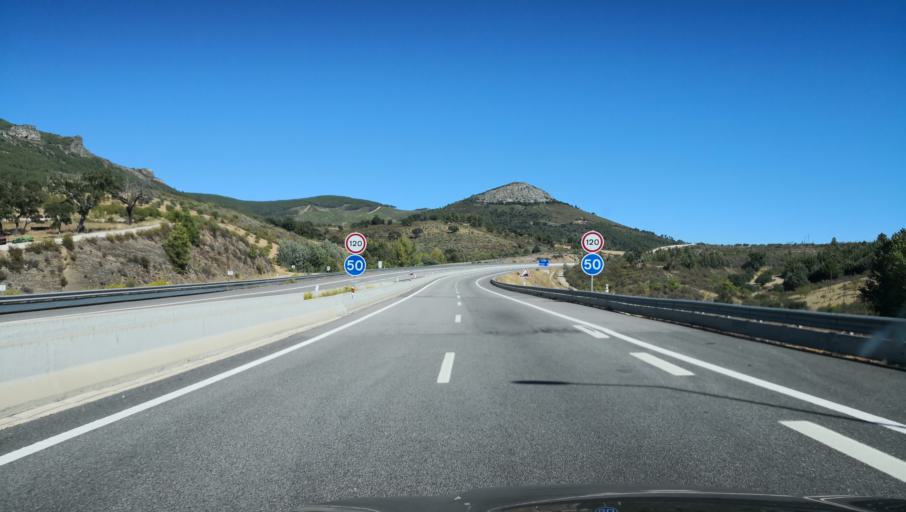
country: PT
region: Vila Real
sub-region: Murca
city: Murca
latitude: 41.4325
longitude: -7.3390
